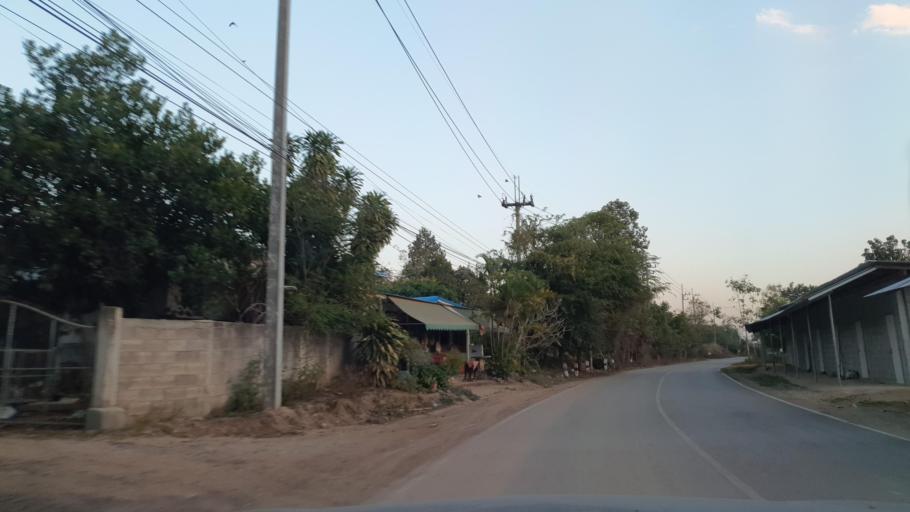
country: TH
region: Chiang Mai
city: Mae Wang
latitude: 18.6385
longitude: 98.7980
